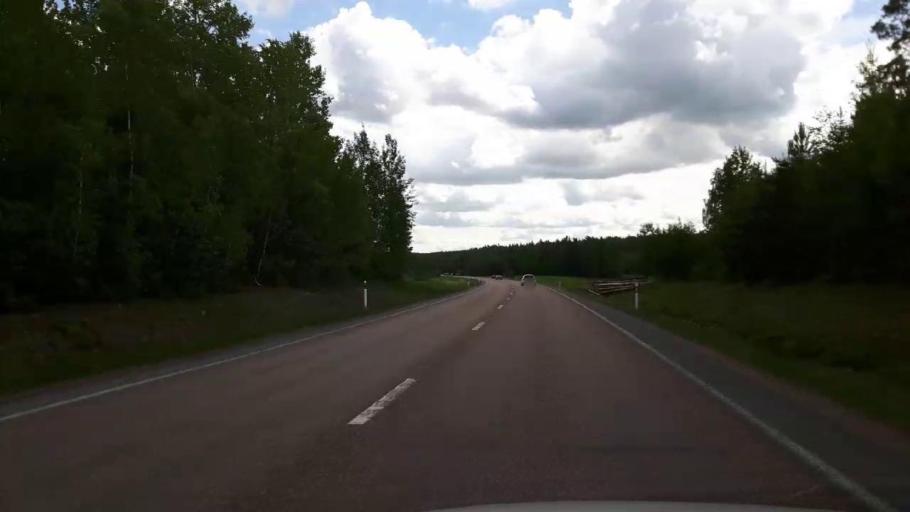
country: SE
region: Dalarna
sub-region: Faluns Kommun
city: Falun
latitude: 60.5031
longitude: 15.7424
